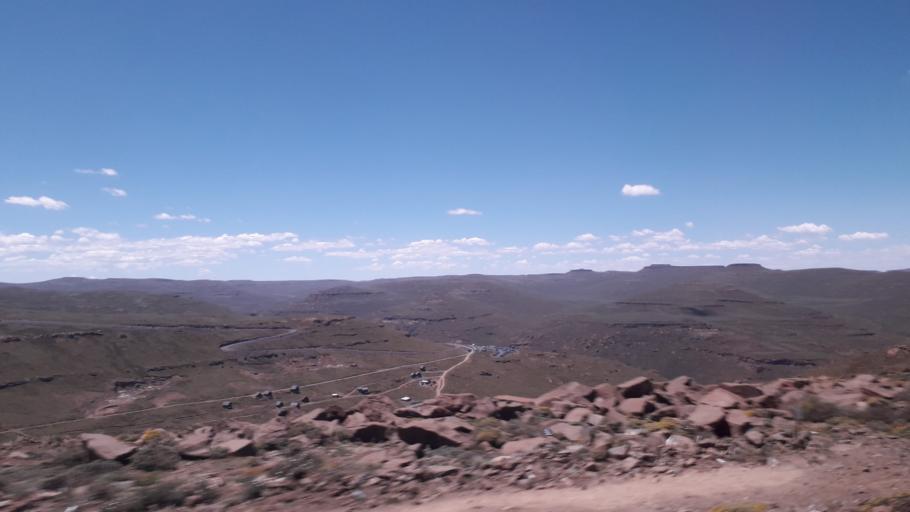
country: ZA
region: Orange Free State
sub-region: Thabo Mofutsanyana District Municipality
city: Phuthaditjhaba
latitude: -28.8153
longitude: 28.7205
